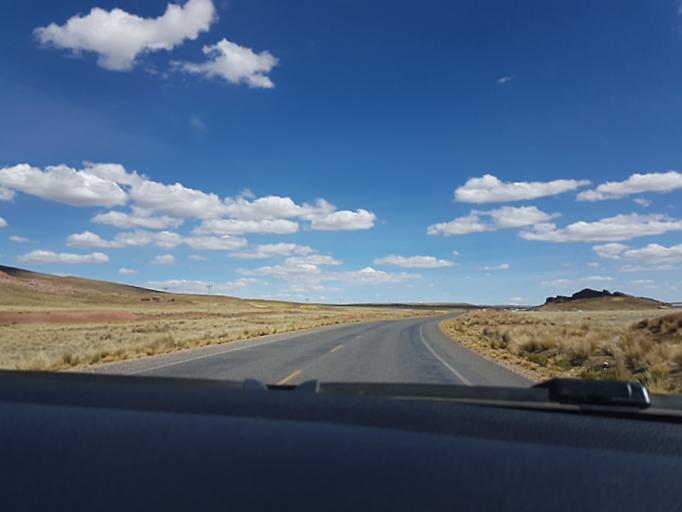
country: BO
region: La Paz
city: Tiahuanaco
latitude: -17.0182
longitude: -68.4299
